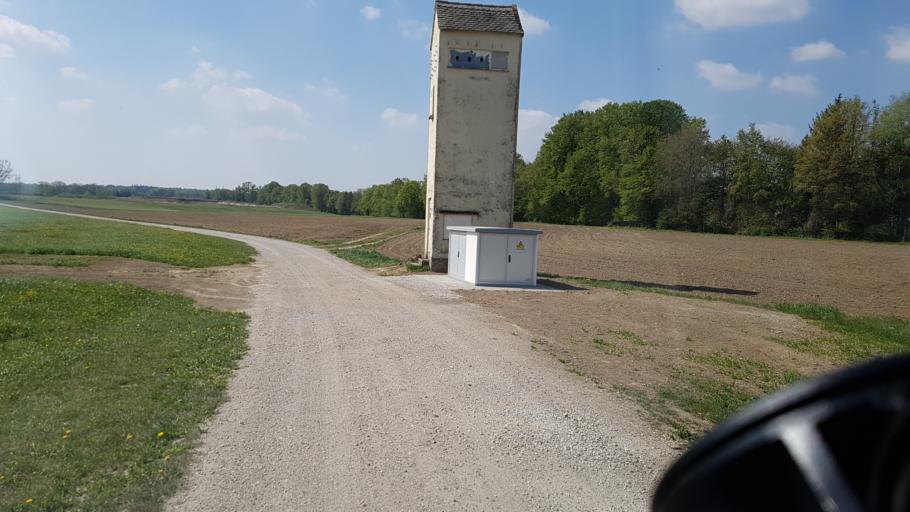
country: DE
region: Bavaria
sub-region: Upper Bavaria
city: Perach
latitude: 48.2597
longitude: 12.8031
